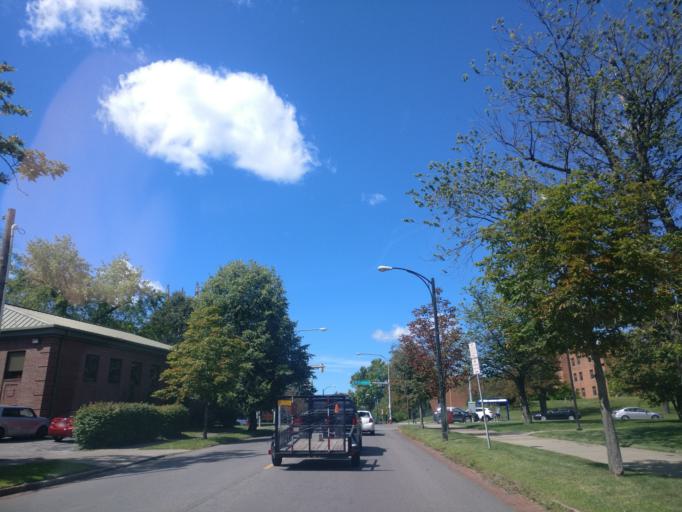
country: US
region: New York
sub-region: Erie County
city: Buffalo
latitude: 42.9113
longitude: -78.8695
